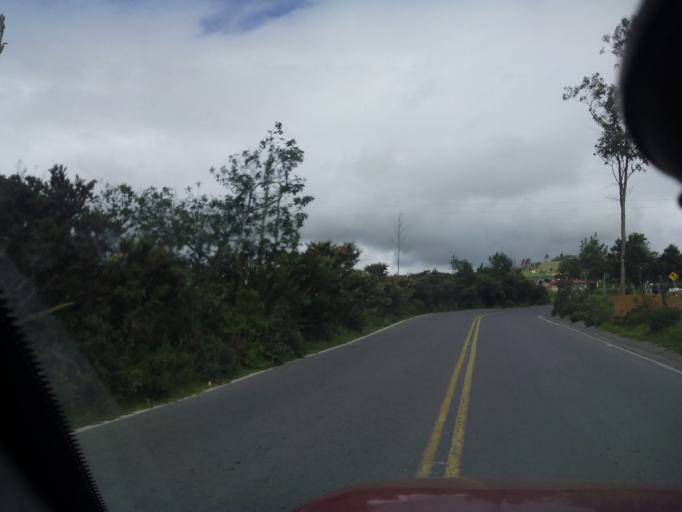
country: CO
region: Boyaca
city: Combita
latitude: 5.6304
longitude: -73.3311
